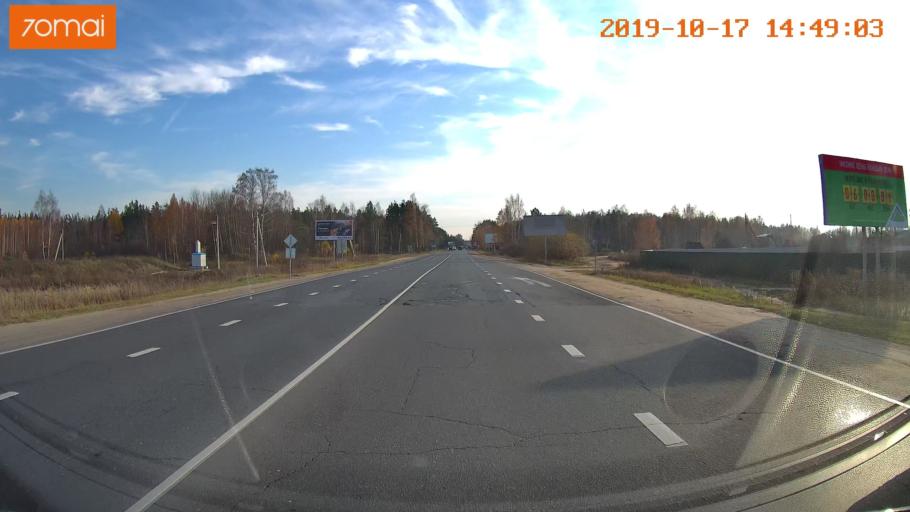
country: RU
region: Rjazan
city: Polyany
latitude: 54.7522
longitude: 39.8387
